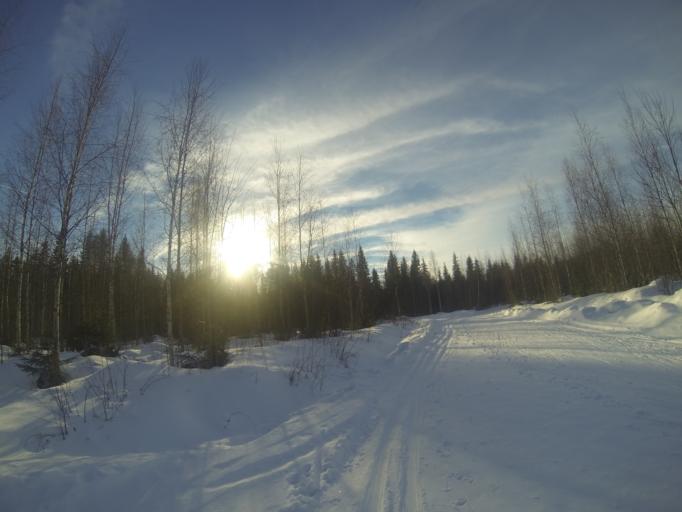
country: FI
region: Southern Savonia
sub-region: Savonlinna
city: Savonlinna
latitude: 61.9322
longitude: 28.9136
